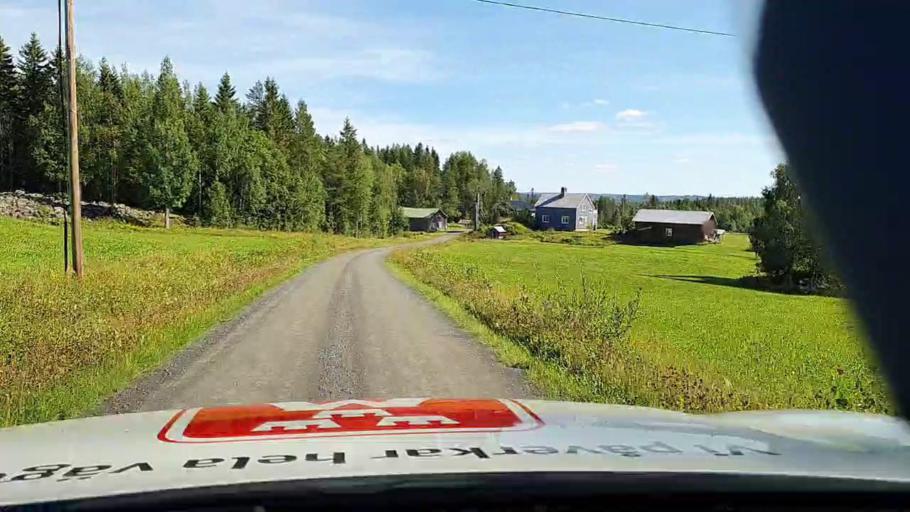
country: SE
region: Jaemtland
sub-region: OEstersunds Kommun
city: Lit
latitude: 63.7745
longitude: 14.6508
